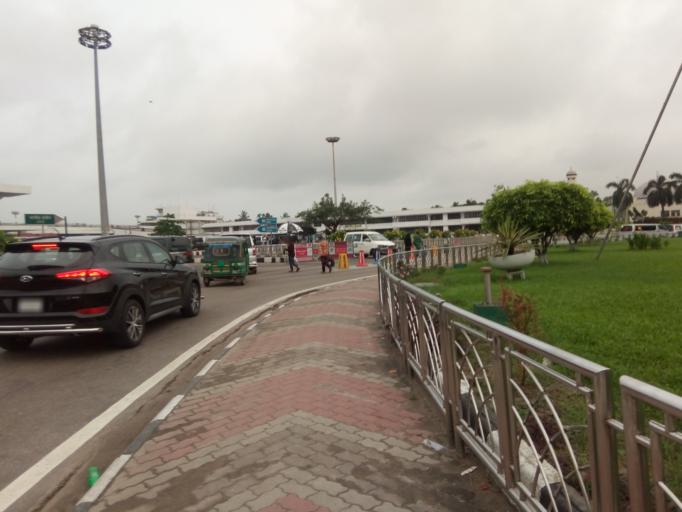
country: BD
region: Dhaka
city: Tungi
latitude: 23.8490
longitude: 90.4066
